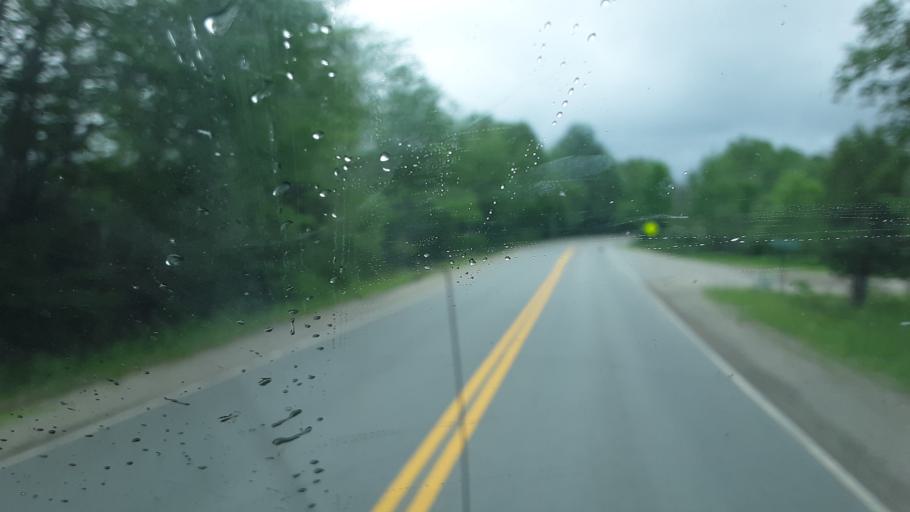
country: US
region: Maine
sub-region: Penobscot County
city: Millinocket
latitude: 45.6868
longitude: -68.7767
